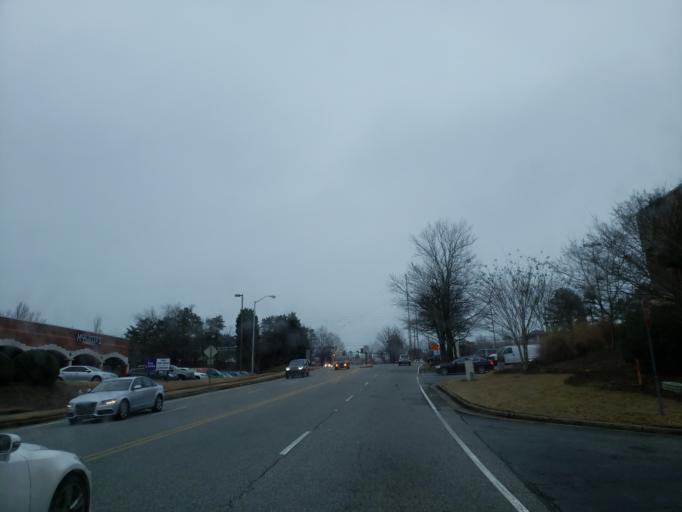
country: US
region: Georgia
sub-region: Fulton County
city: Roswell
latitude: 34.0184
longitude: -84.3184
